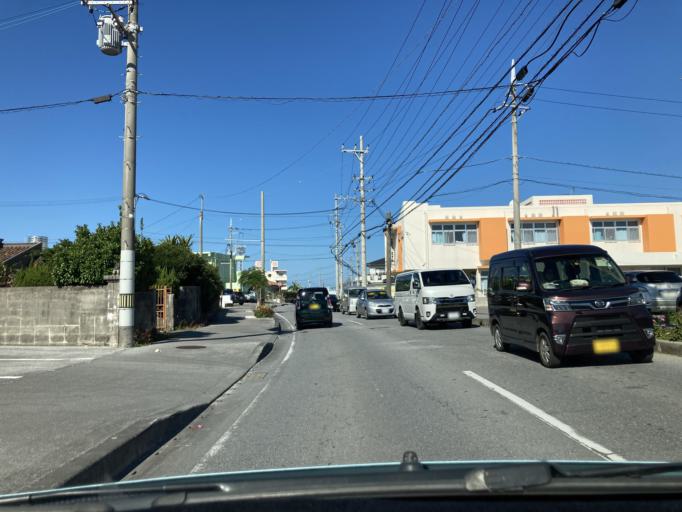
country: JP
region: Okinawa
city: Okinawa
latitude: 26.3596
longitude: 127.8254
